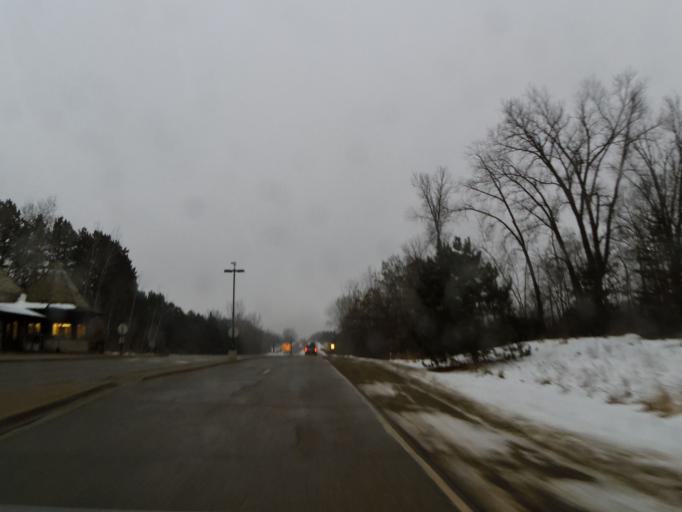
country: US
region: Minnesota
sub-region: Washington County
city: Lake Elmo
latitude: 44.9711
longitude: -92.9035
